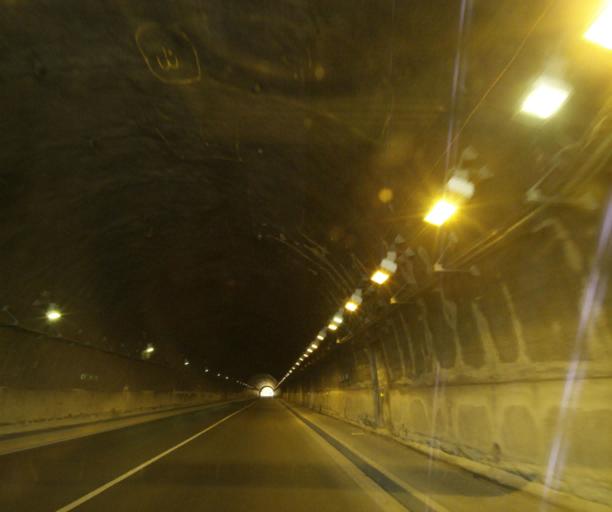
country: FR
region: Provence-Alpes-Cote d'Azur
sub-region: Departement des Bouches-du-Rhone
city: Le Rove
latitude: 43.3548
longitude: 5.2810
